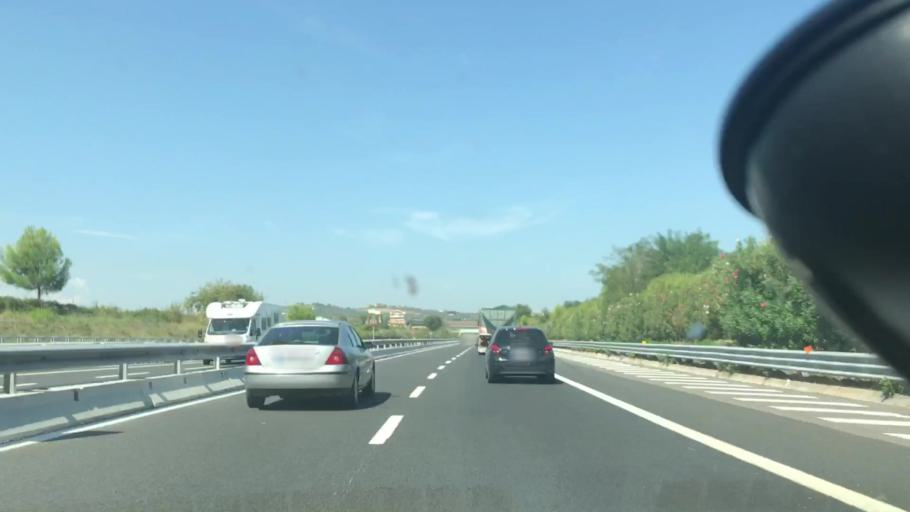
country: IT
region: Abruzzo
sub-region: Provincia di Chieti
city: San Salvo
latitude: 42.0552
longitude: 14.7494
